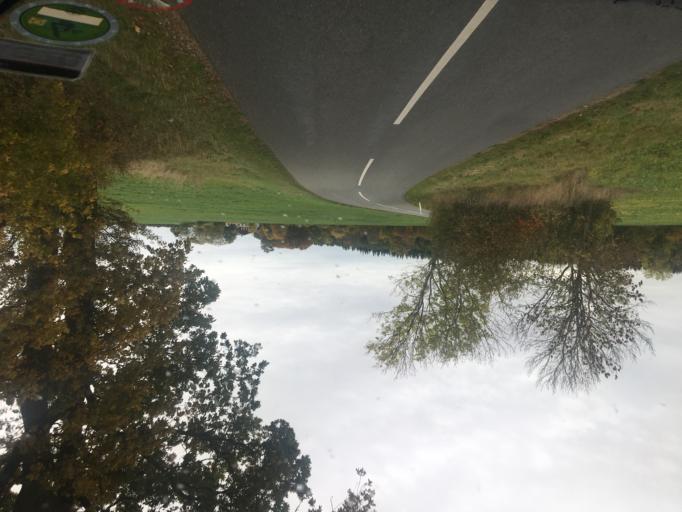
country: DK
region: Zealand
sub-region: Koge Kommune
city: Bjaeverskov
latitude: 55.4119
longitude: 11.9840
